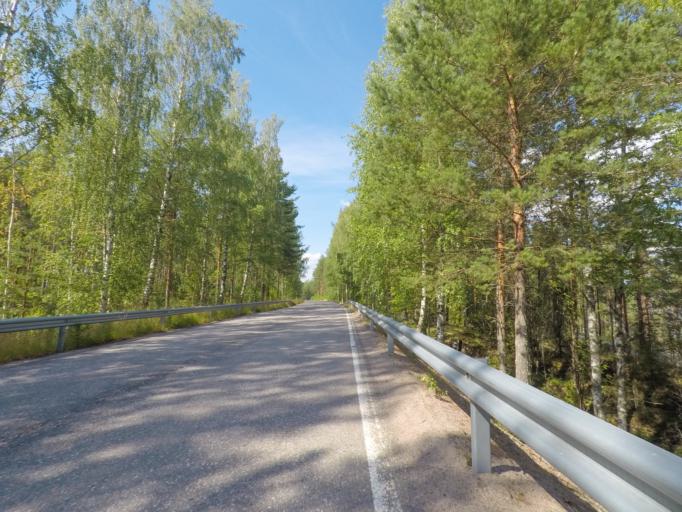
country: FI
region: Southern Savonia
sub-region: Mikkeli
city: Puumala
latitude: 61.4692
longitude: 28.1687
